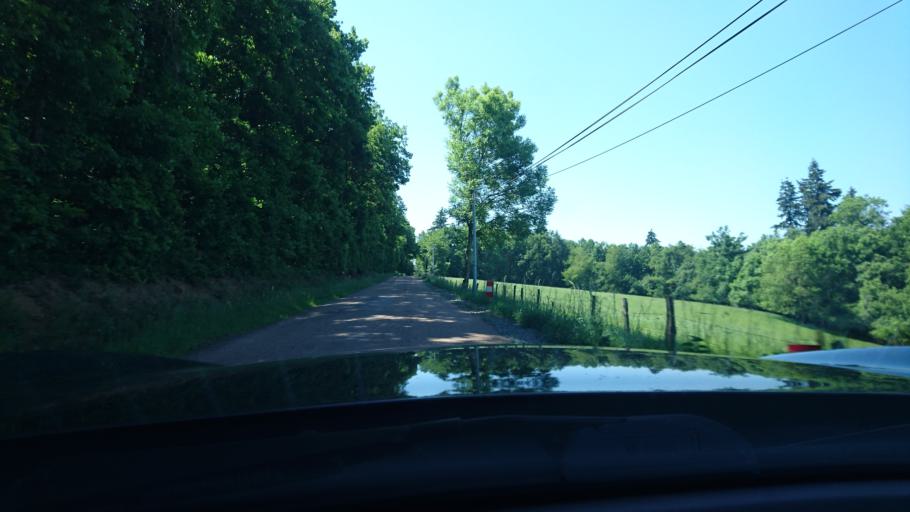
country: FR
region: Rhone-Alpes
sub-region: Departement de la Loire
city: Bussieres
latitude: 45.8528
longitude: 4.2594
